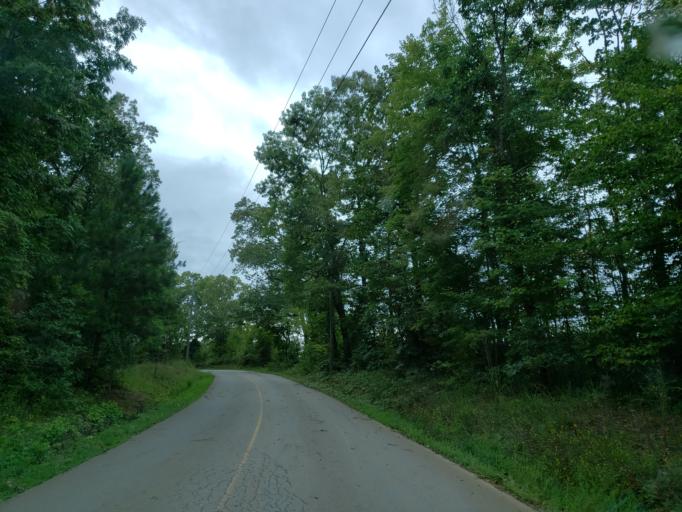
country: US
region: Georgia
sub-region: Pickens County
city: Jasper
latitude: 34.5514
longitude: -84.5169
